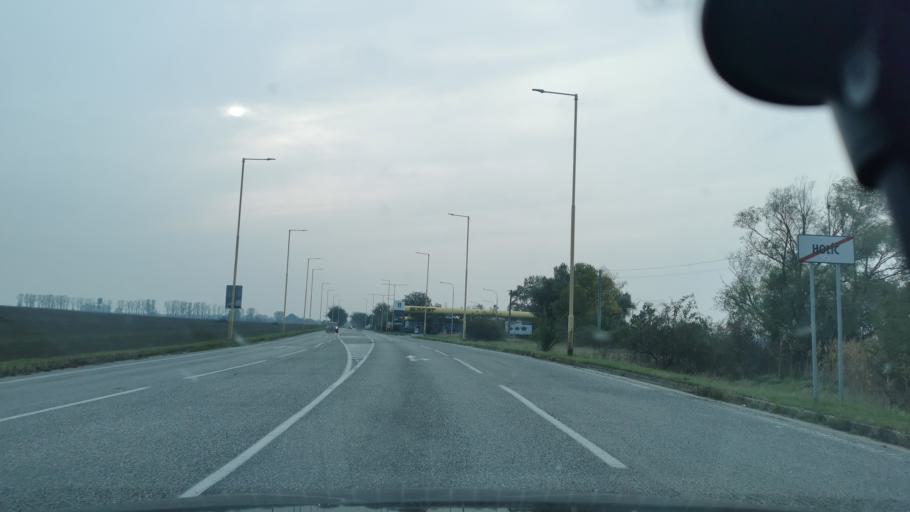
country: SK
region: Trnavsky
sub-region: Okres Skalica
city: Holic
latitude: 48.8005
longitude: 17.1499
